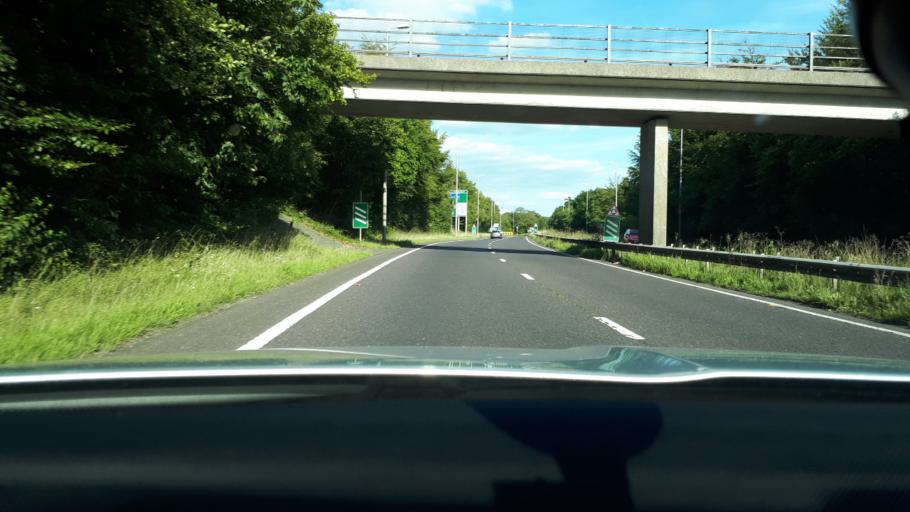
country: GB
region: England
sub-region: Kent
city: Halstead
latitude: 51.3471
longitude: 0.1309
